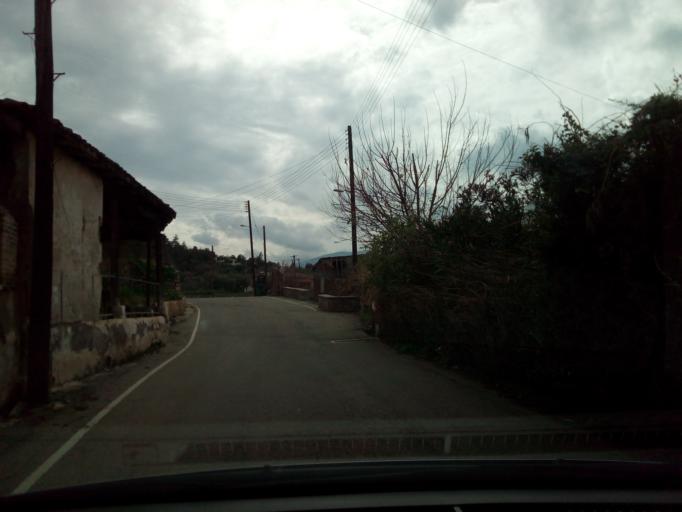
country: CY
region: Lefkosia
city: Lefka
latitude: 35.0719
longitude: 32.8908
